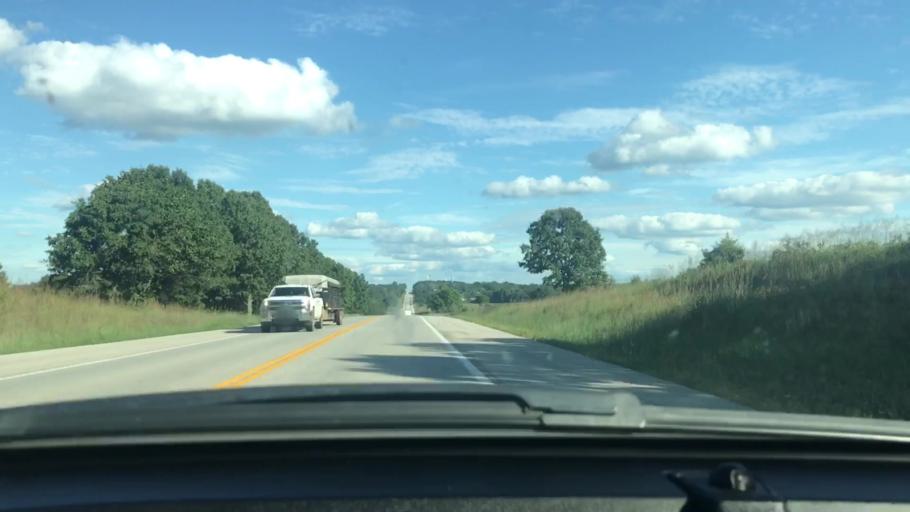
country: US
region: Missouri
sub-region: Howell County
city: West Plains
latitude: 36.6601
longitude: -91.7077
